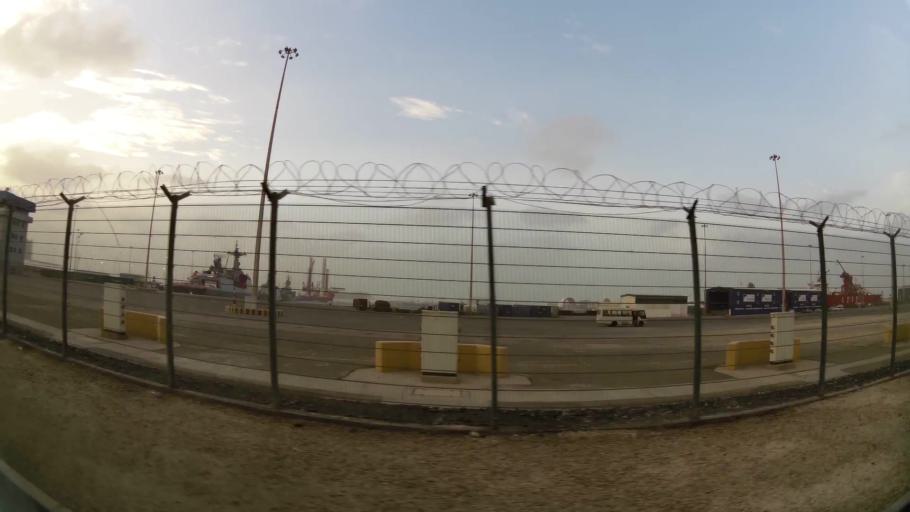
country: AE
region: Abu Dhabi
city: Abu Dhabi
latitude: 24.5155
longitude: 54.3936
